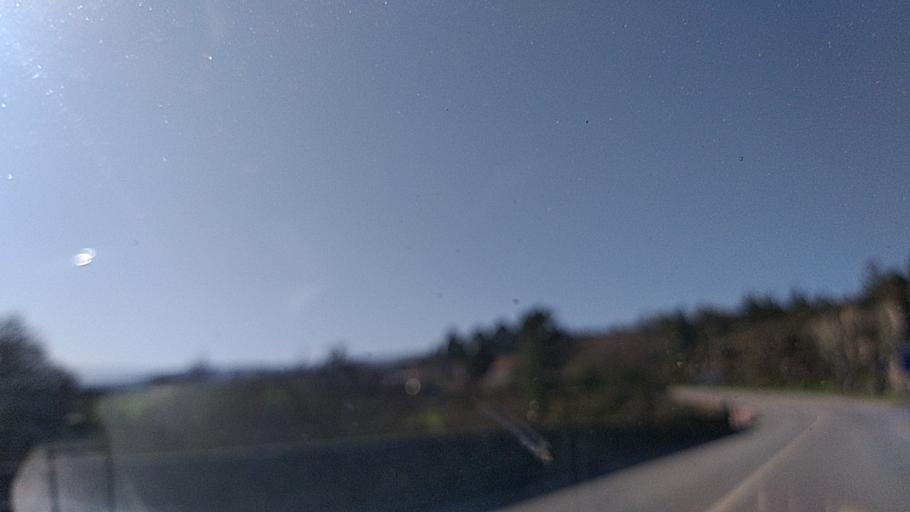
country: PT
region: Guarda
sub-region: Celorico da Beira
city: Celorico da Beira
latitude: 40.6539
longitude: -7.3831
